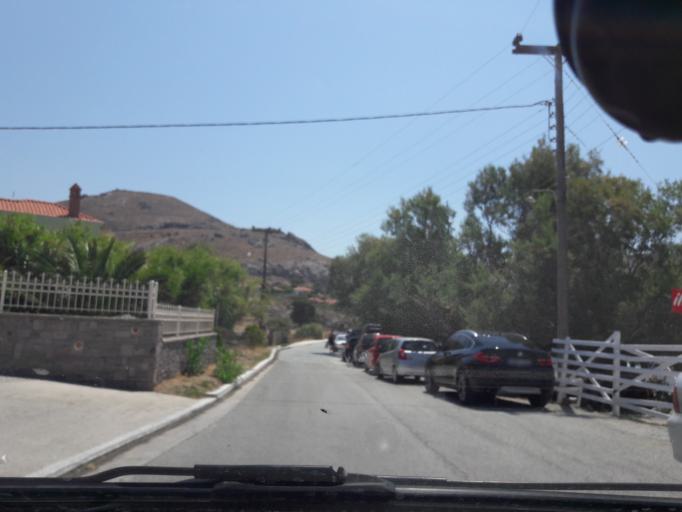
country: GR
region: North Aegean
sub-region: Nomos Lesvou
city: Myrina
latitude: 39.9254
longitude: 25.0680
